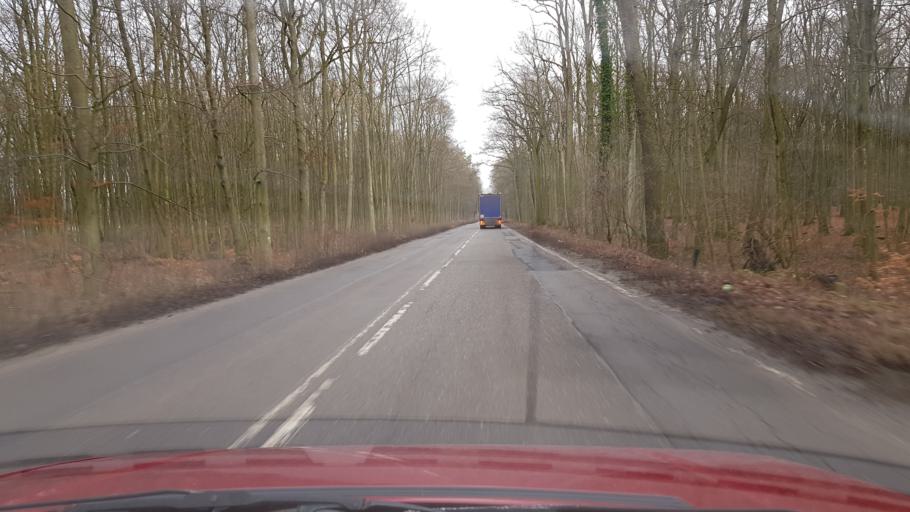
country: PL
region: West Pomeranian Voivodeship
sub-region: Powiat policki
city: Police
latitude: 53.5304
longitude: 14.5737
